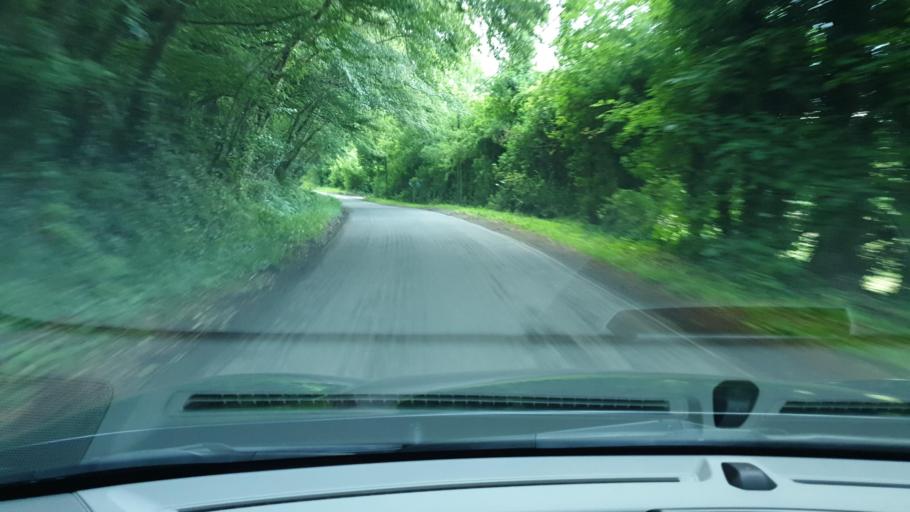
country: IE
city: Kentstown
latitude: 53.5774
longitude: -6.5169
